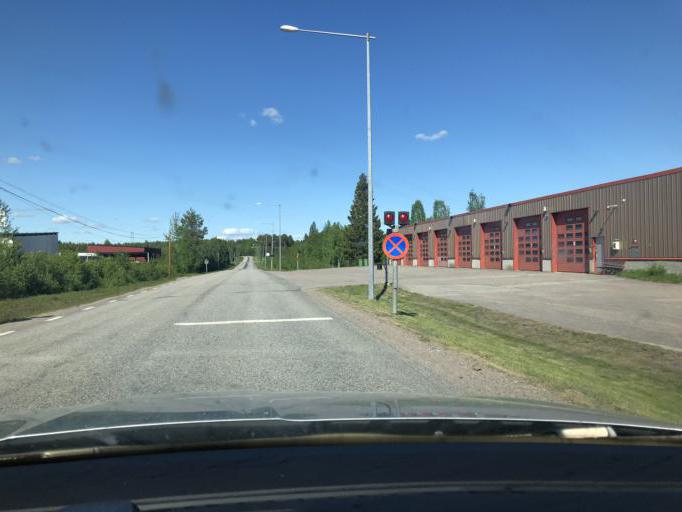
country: SE
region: Norrbotten
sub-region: Kalix Kommun
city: Kalix
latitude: 65.8697
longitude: 23.1467
